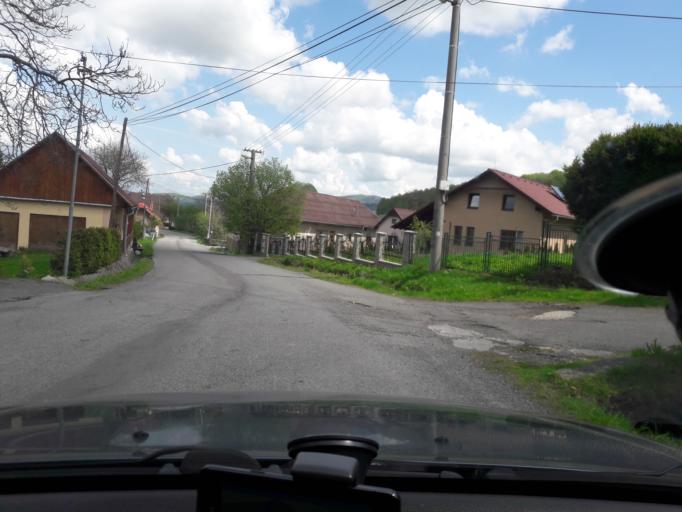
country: SK
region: Banskobystricky
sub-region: Okres Banska Bystrica
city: Zvolen
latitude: 48.4939
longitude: 19.2796
